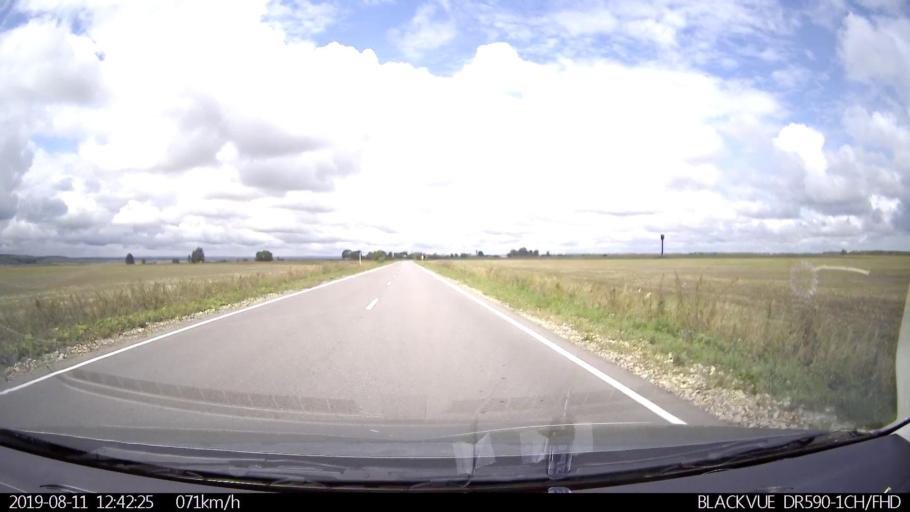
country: RU
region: Ulyanovsk
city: Ignatovka
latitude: 53.8457
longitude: 47.7517
